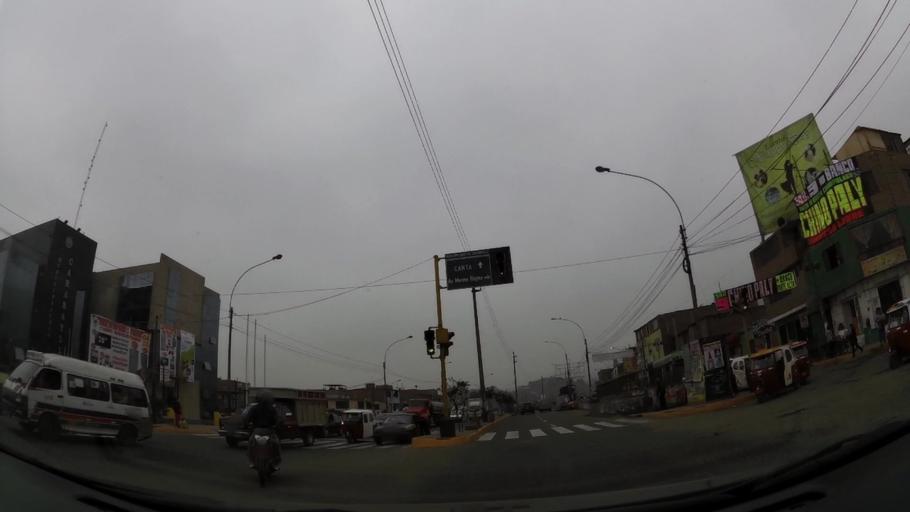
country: PE
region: Lima
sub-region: Lima
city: Urb. Santo Domingo
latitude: -11.8905
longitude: -77.0269
